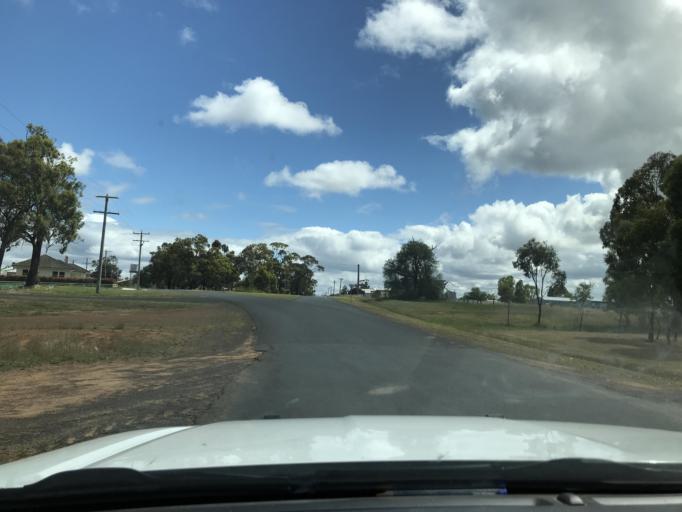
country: AU
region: Victoria
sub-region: Horsham
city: Horsham
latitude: -36.7224
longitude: 141.4764
